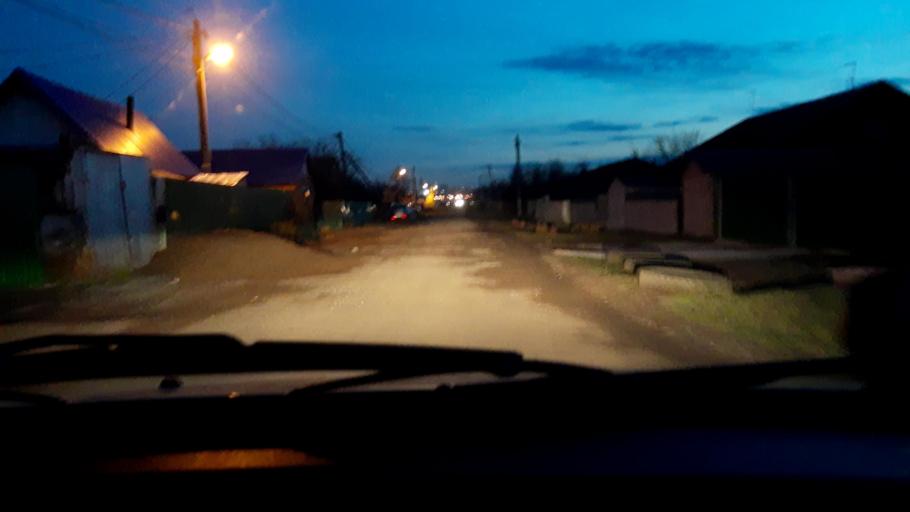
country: RU
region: Bashkortostan
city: Ufa
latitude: 54.7860
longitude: 55.9547
